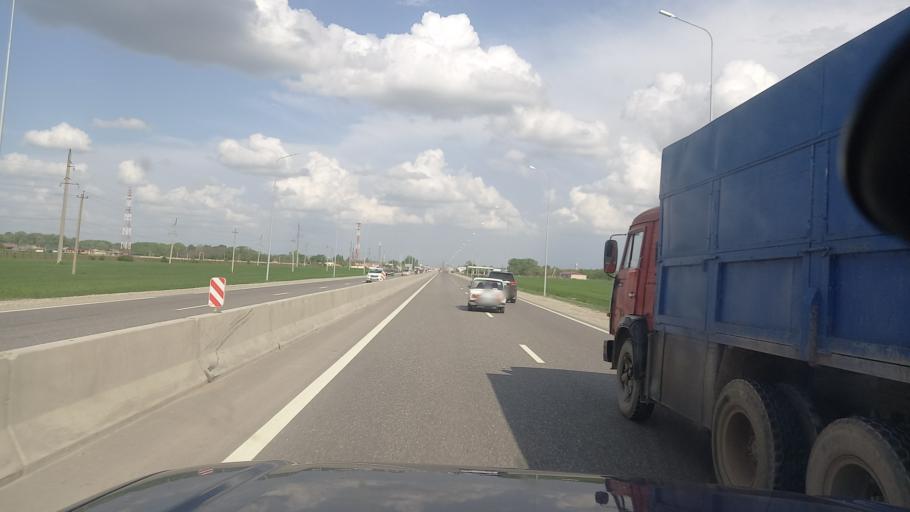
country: RU
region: Chechnya
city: Alkhan-Yurt
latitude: 43.2205
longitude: 45.5420
